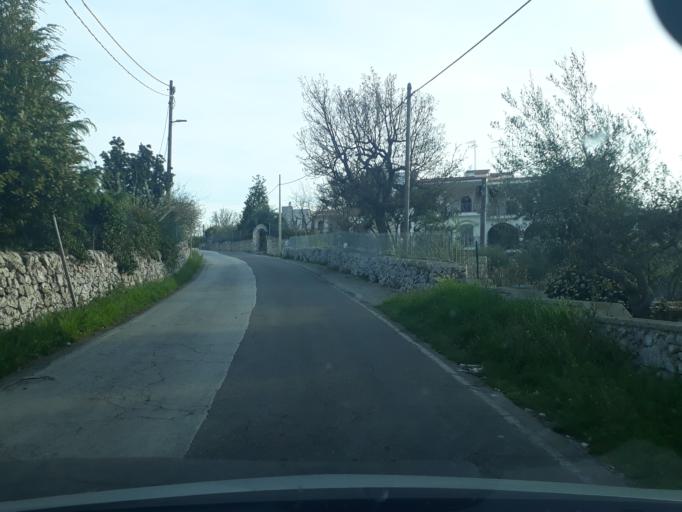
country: IT
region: Apulia
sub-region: Provincia di Brindisi
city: Lamie di Olimpie-Selva
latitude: 40.8294
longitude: 17.3323
